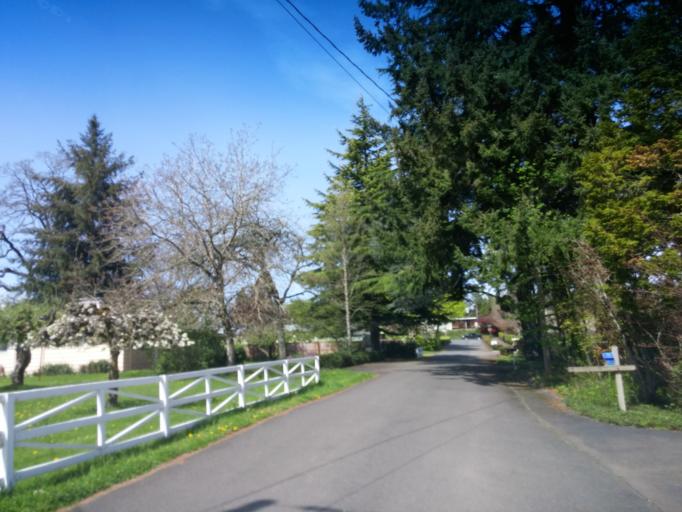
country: US
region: Oregon
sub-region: Washington County
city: Cedar Mill
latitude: 45.5248
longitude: -122.8038
